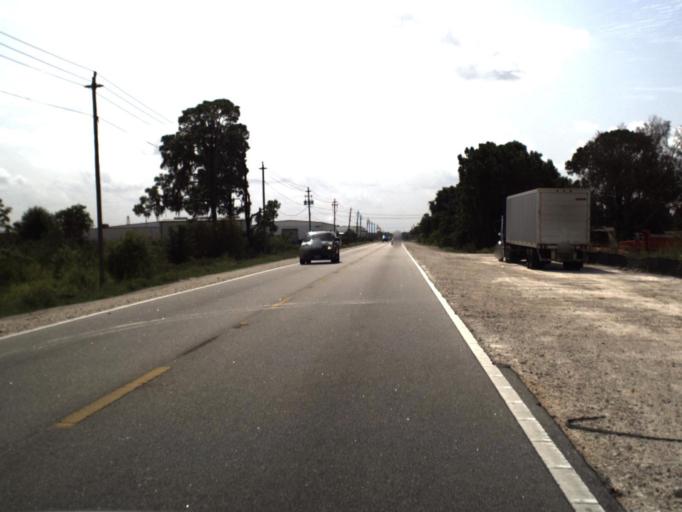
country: US
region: Florida
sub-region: Polk County
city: Auburndale
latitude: 28.0434
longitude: -81.7870
